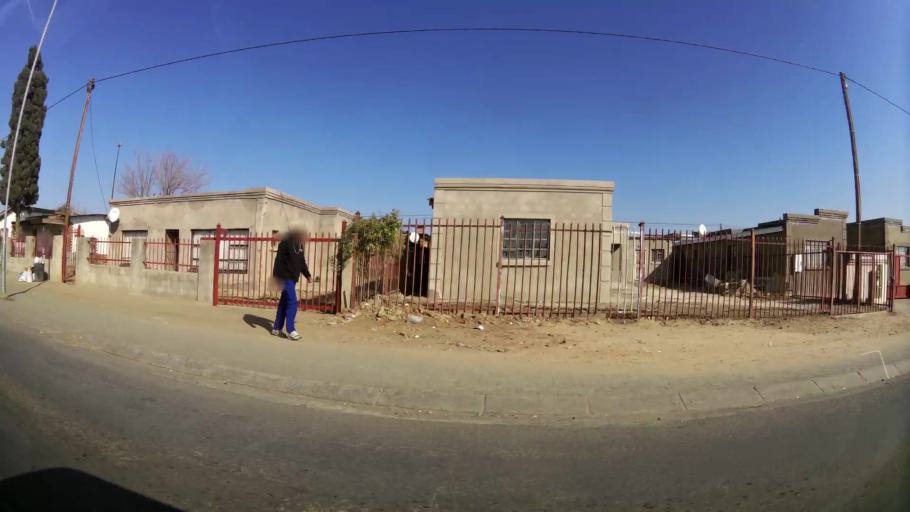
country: ZA
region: Orange Free State
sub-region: Mangaung Metropolitan Municipality
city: Bloemfontein
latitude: -29.1551
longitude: 26.2414
